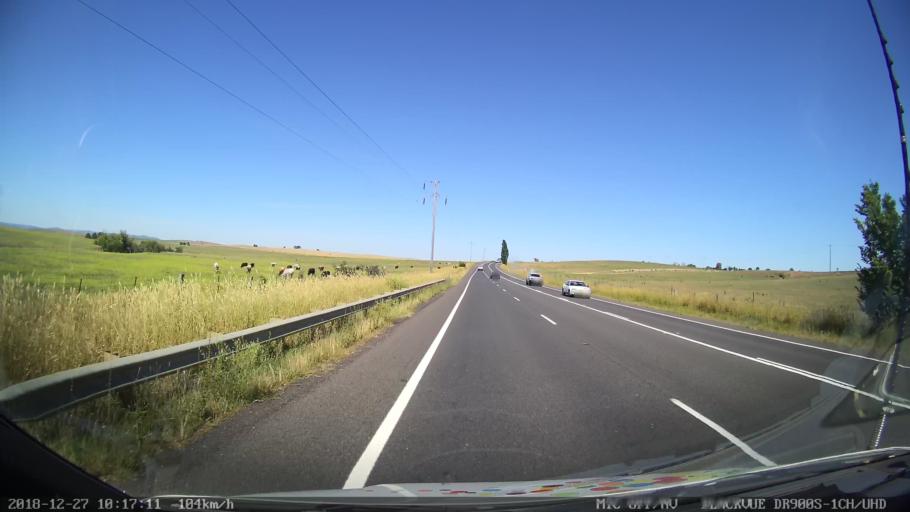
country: AU
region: New South Wales
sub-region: Bathurst Regional
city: Kelso
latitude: -33.4261
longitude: 149.6823
